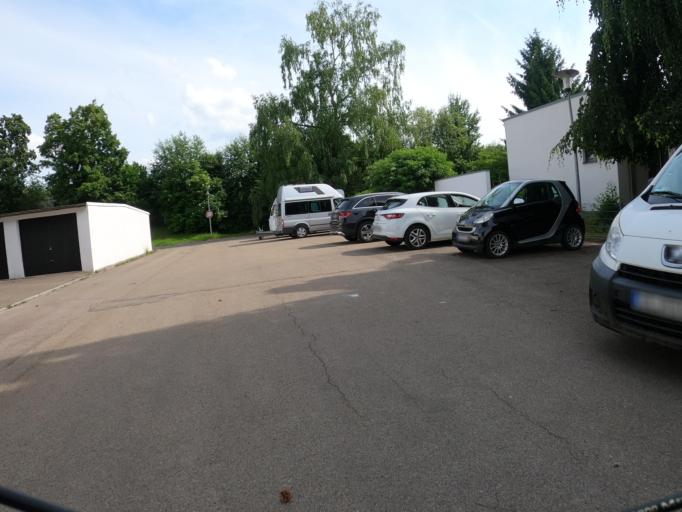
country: DE
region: Baden-Wuerttemberg
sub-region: Tuebingen Region
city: Ulm
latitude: 48.3816
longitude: 9.9962
